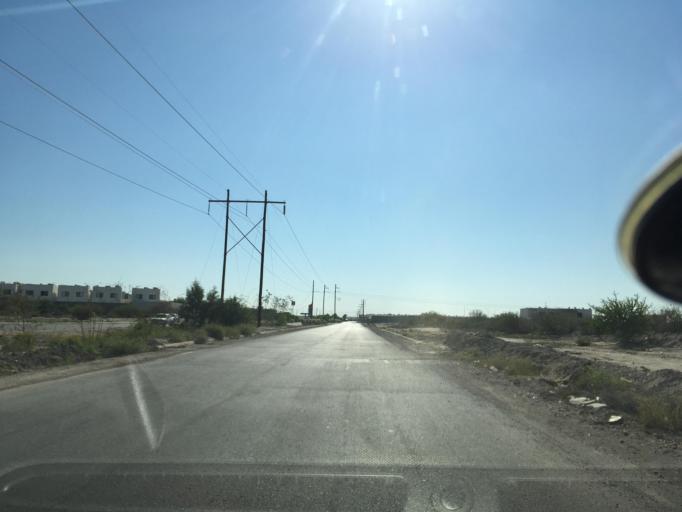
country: MX
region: Coahuila
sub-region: Torreon
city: Fraccionamiento la Noria
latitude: 25.5737
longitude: -103.3713
